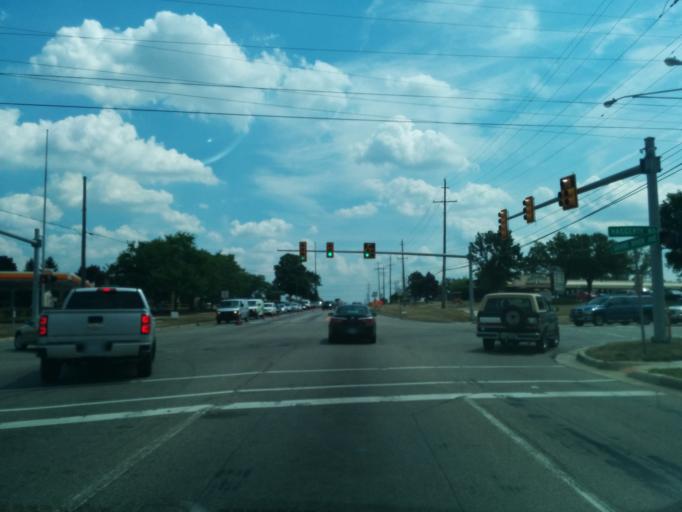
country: US
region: Michigan
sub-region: Oakland County
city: Novi
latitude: 42.4718
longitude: -83.4355
